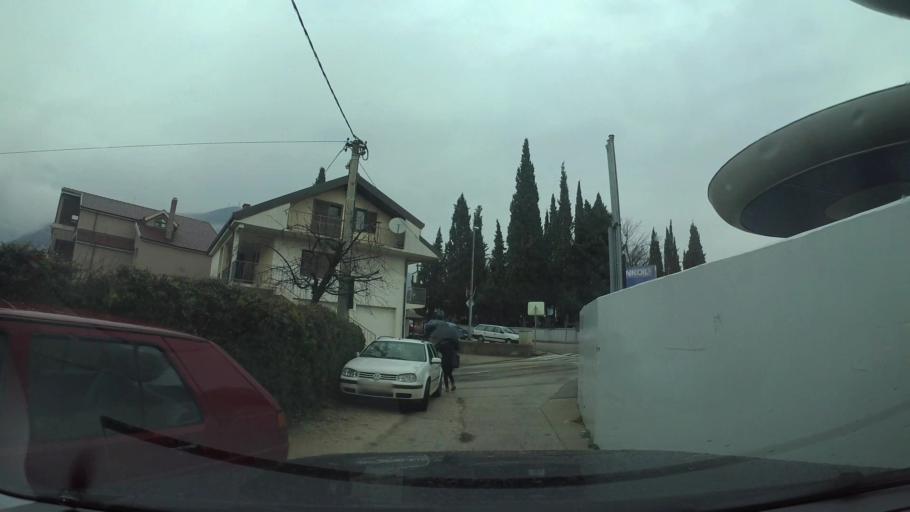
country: BA
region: Federation of Bosnia and Herzegovina
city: Cim
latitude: 43.3476
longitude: 17.7865
